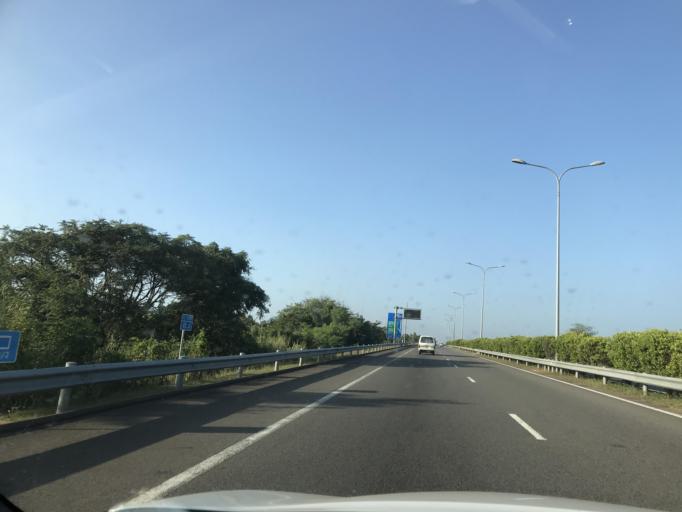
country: LK
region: Western
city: Ja Ela
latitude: 7.0737
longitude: 79.8779
